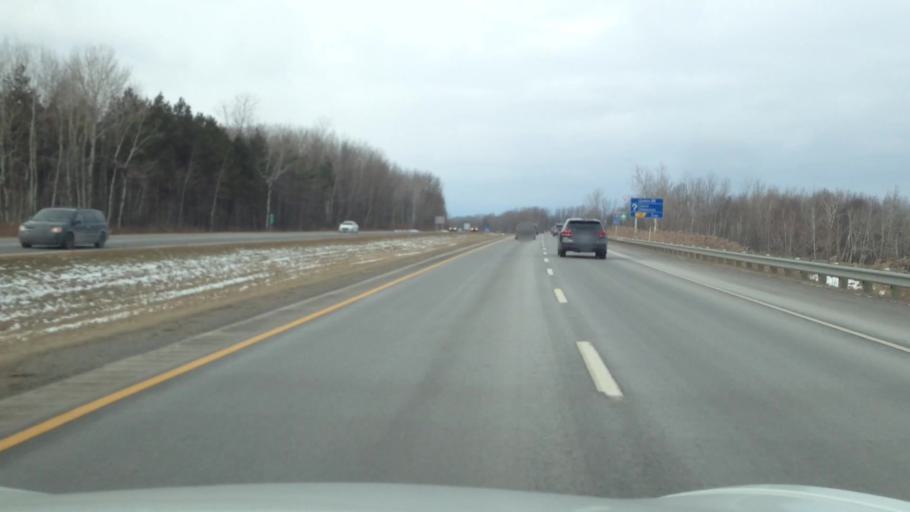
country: CA
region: Quebec
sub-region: Monteregie
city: Rigaud
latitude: 45.4639
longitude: -74.2372
